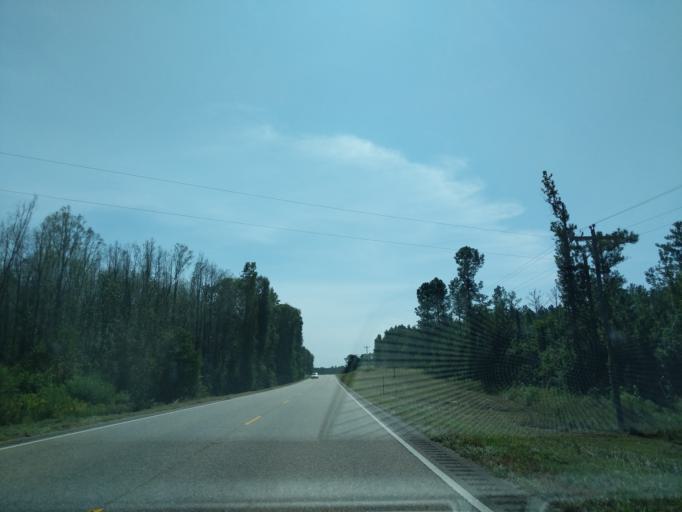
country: US
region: Alabama
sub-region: Covington County
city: Florala
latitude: 31.0628
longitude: -86.5749
